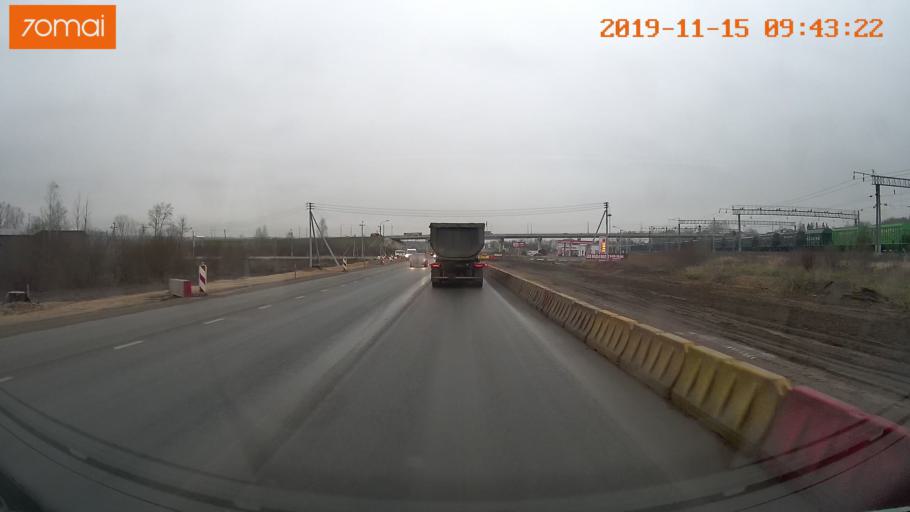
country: RU
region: Vologda
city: Sheksna
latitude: 59.2100
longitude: 38.5102
